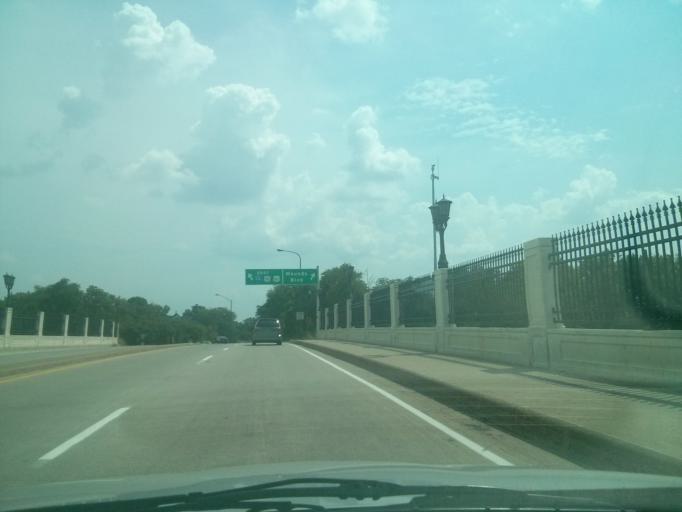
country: US
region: Minnesota
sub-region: Ramsey County
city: Saint Paul
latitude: 44.9525
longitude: -93.0700
